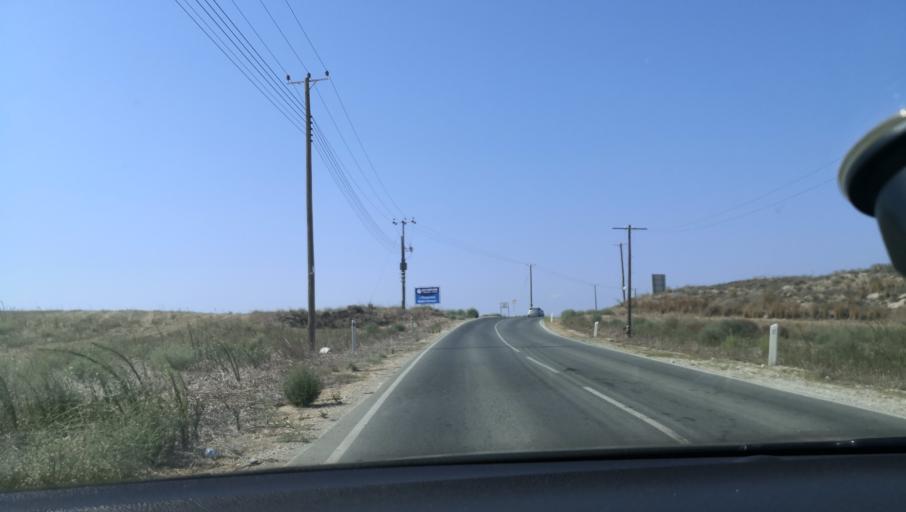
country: CY
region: Lefkosia
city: Kato Deftera
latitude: 35.1208
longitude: 33.2650
